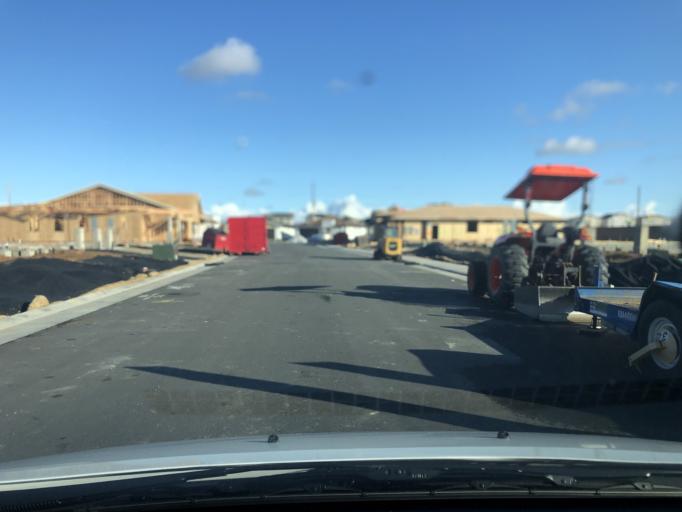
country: US
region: California
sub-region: Sacramento County
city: Antelope
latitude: 38.7714
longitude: -121.3872
